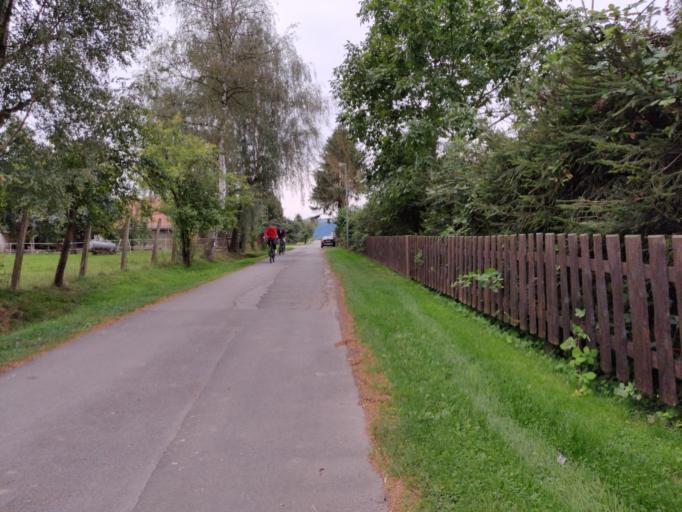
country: DE
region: Lower Saxony
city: Bodenwerder
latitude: 51.9588
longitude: 9.5052
